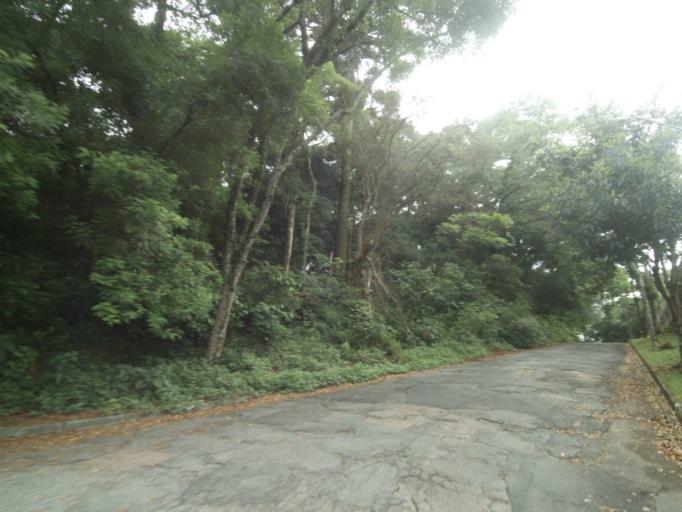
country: BR
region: Parana
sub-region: Curitiba
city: Curitiba
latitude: -25.4113
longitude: -49.3058
